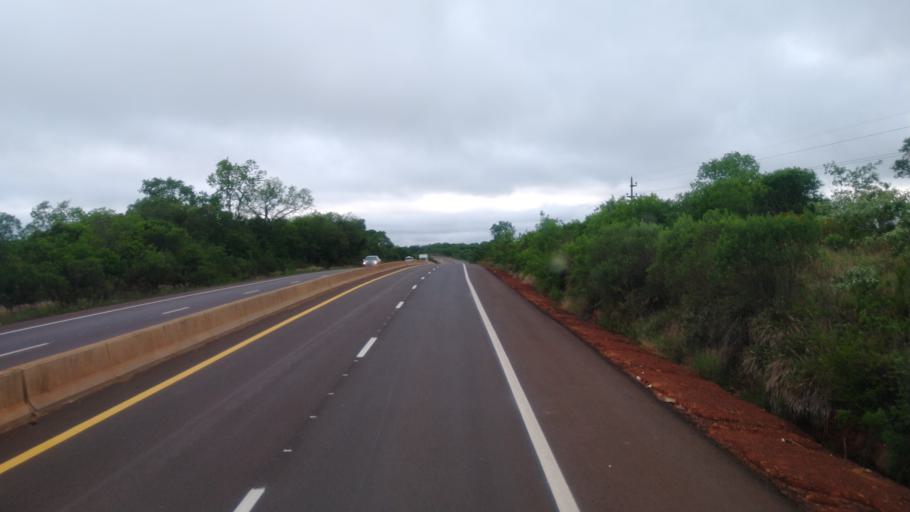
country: AR
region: Misiones
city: Santa Ana
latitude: -27.4248
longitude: -55.6225
